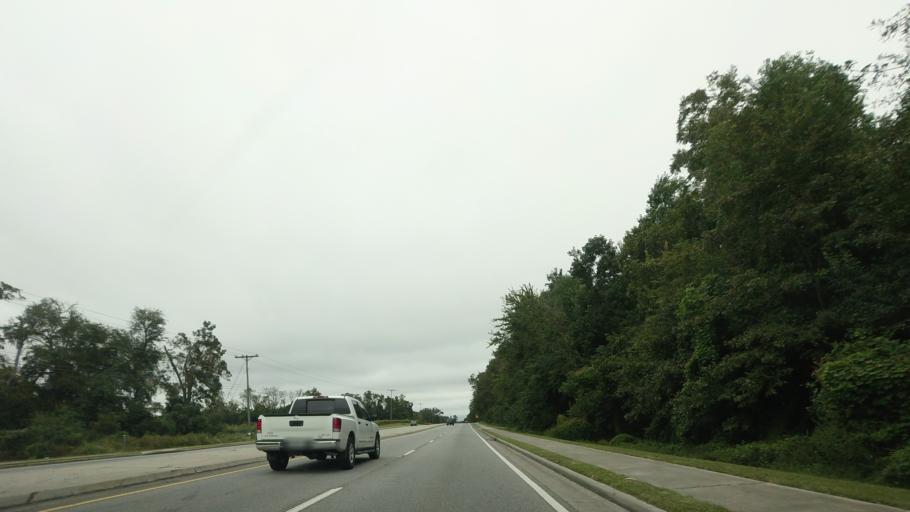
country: US
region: Georgia
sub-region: Lowndes County
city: Valdosta
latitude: 30.8938
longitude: -83.2692
